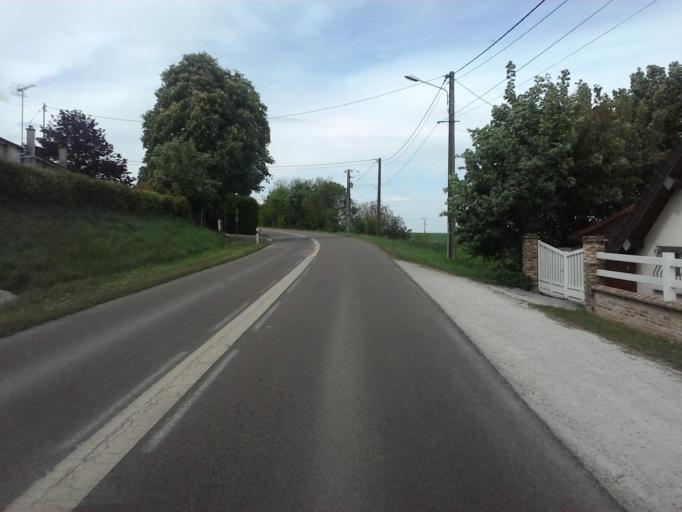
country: FR
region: Champagne-Ardenne
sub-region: Departement de l'Aube
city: Bouilly
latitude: 48.1733
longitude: 4.0179
